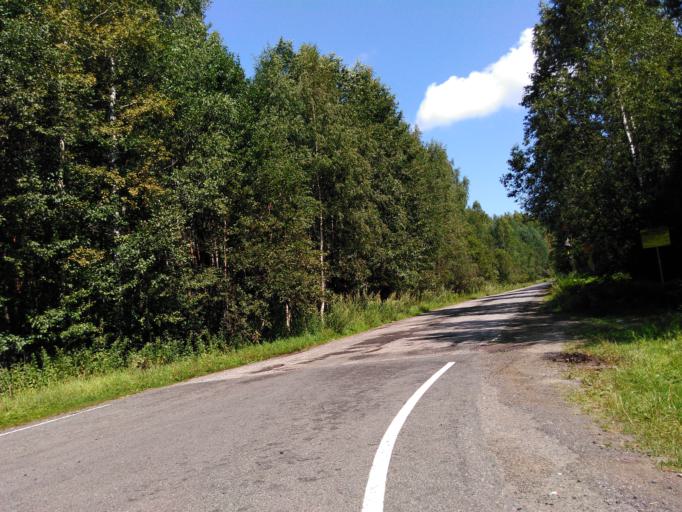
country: RU
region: Moskovskaya
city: Elektrogorsk
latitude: 56.0230
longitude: 38.7616
